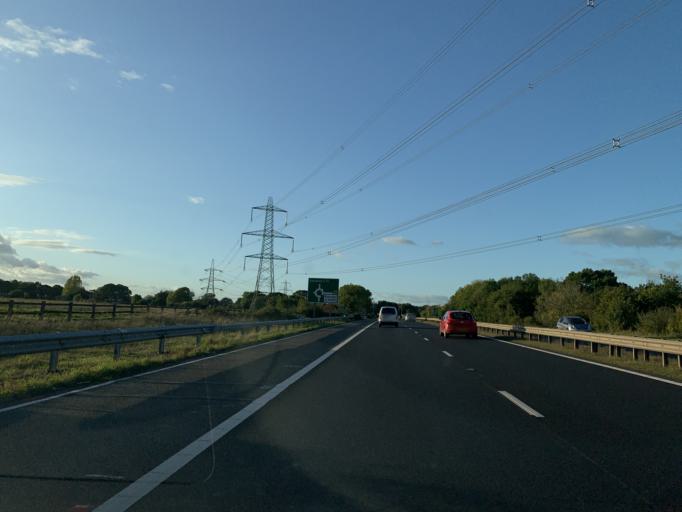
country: GB
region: England
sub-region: Hampshire
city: Romsey
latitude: 50.9509
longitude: -1.5316
